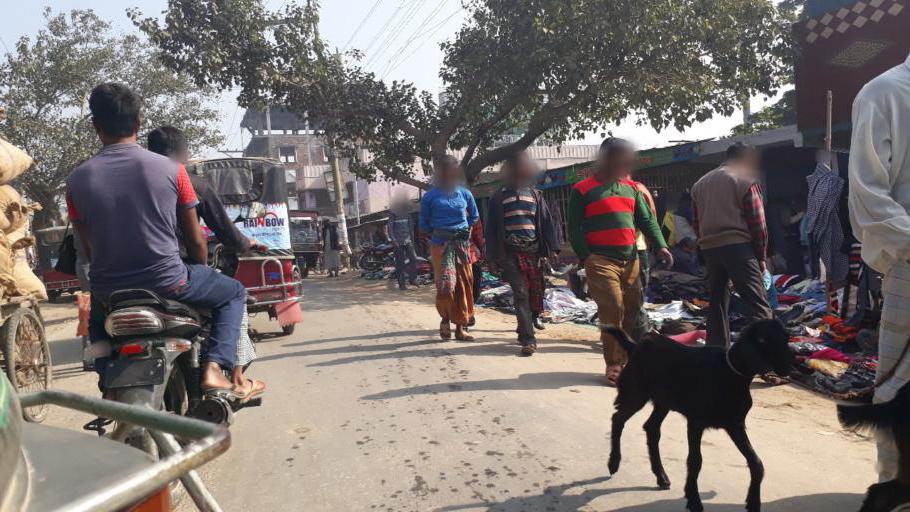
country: BD
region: Khulna
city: Kushtia
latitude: 23.8617
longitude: 89.0375
